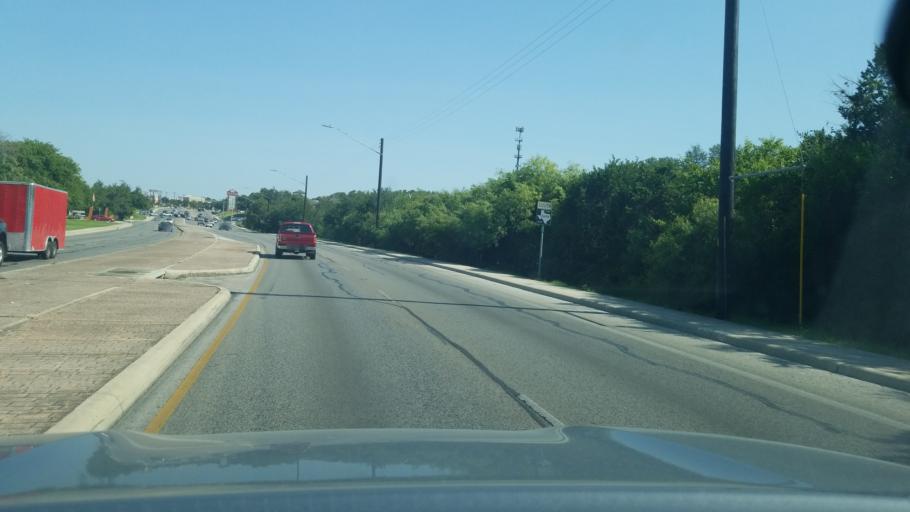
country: US
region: Texas
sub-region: Bexar County
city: Hollywood Park
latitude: 29.5821
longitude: -98.5158
